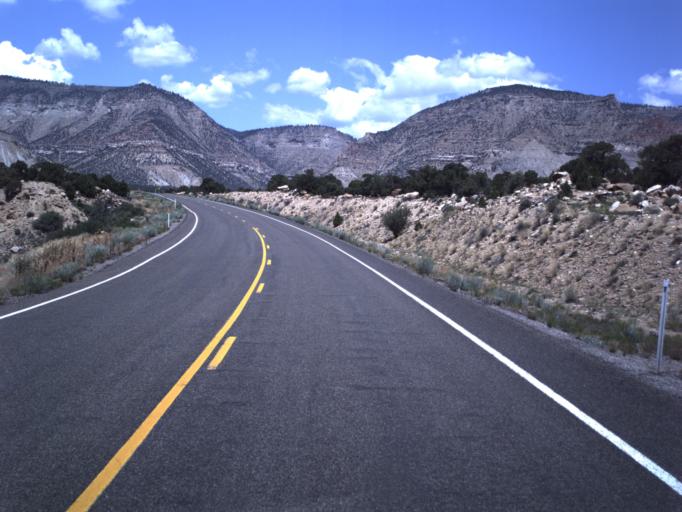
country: US
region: Utah
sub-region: Emery County
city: Orangeville
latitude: 39.2793
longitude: -111.1016
